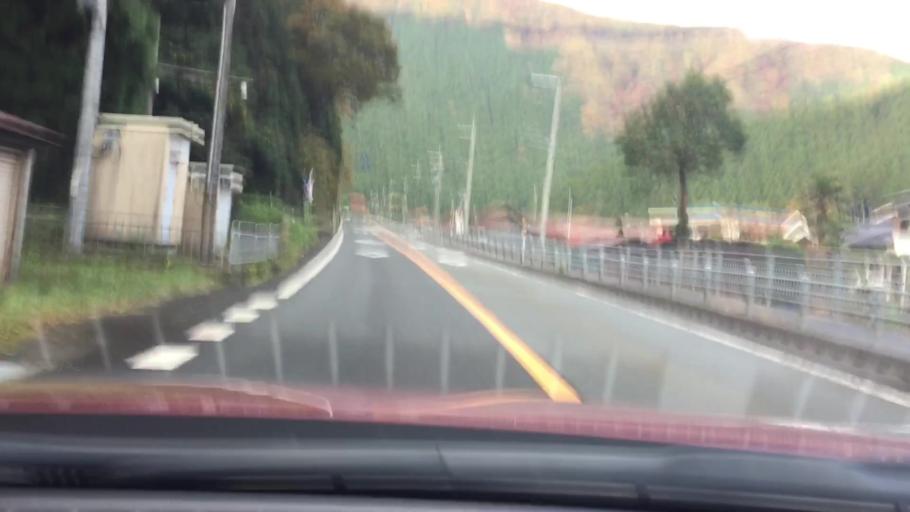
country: JP
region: Hyogo
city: Yamazakicho-nakabirose
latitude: 35.1864
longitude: 134.5318
